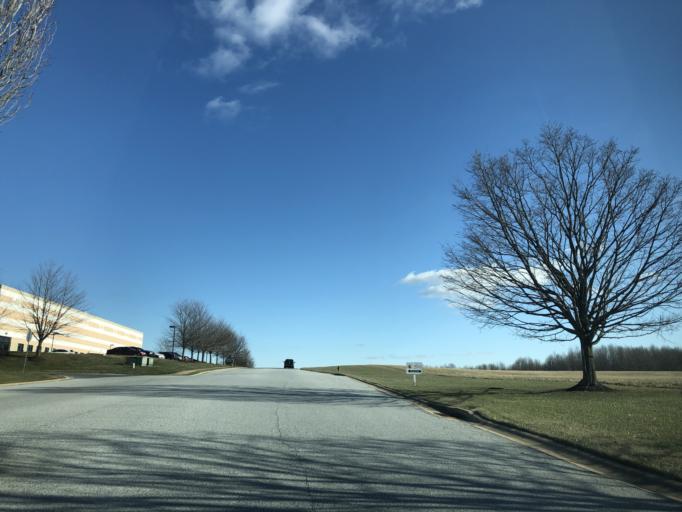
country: US
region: Pennsylvania
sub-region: Chester County
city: Coatesville
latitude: 39.9913
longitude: -75.8717
